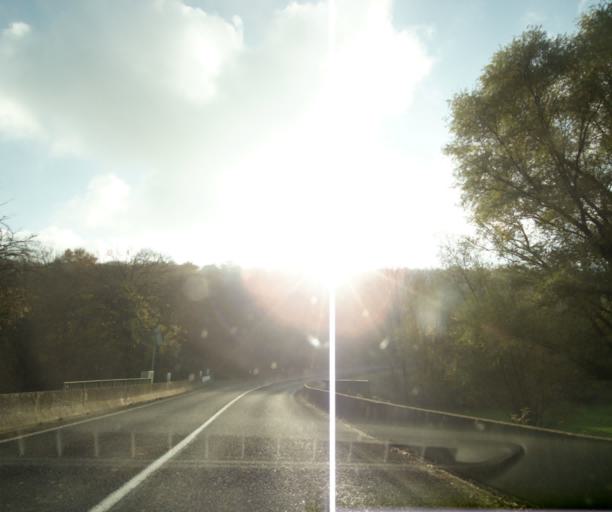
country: FR
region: Lorraine
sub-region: Departement de Meurthe-et-Moselle
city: Briey
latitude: 49.2687
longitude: 5.9268
